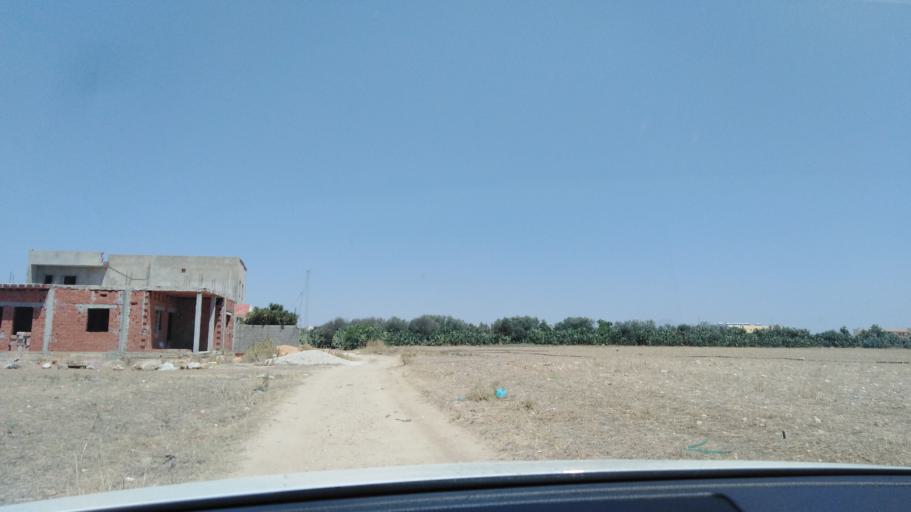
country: TN
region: Al Qayrawan
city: Sbikha
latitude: 36.1094
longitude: 10.0950
